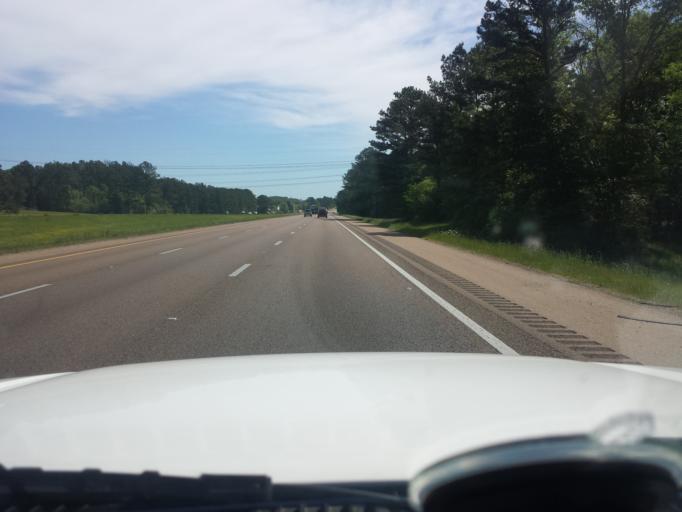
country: US
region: Mississippi
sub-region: Rankin County
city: Pearl
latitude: 32.2667
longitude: -90.0992
